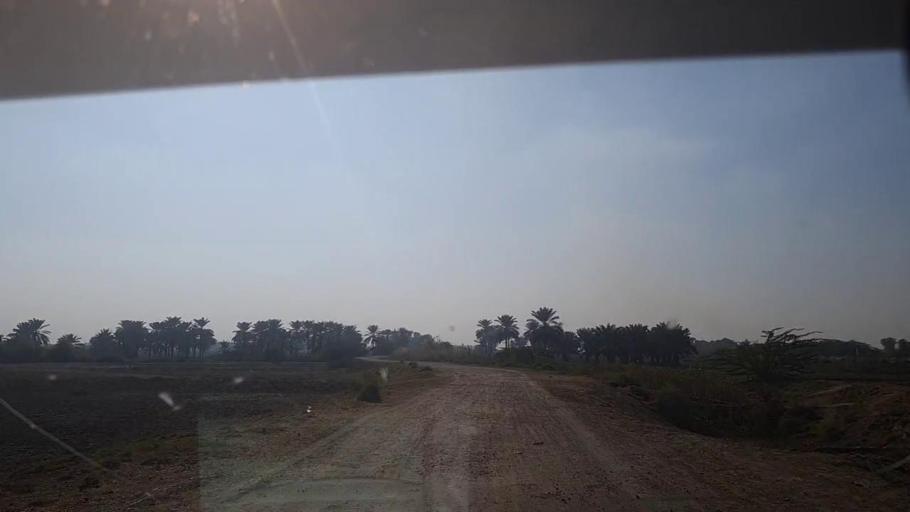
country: PK
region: Sindh
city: Gambat
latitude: 27.3763
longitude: 68.5752
